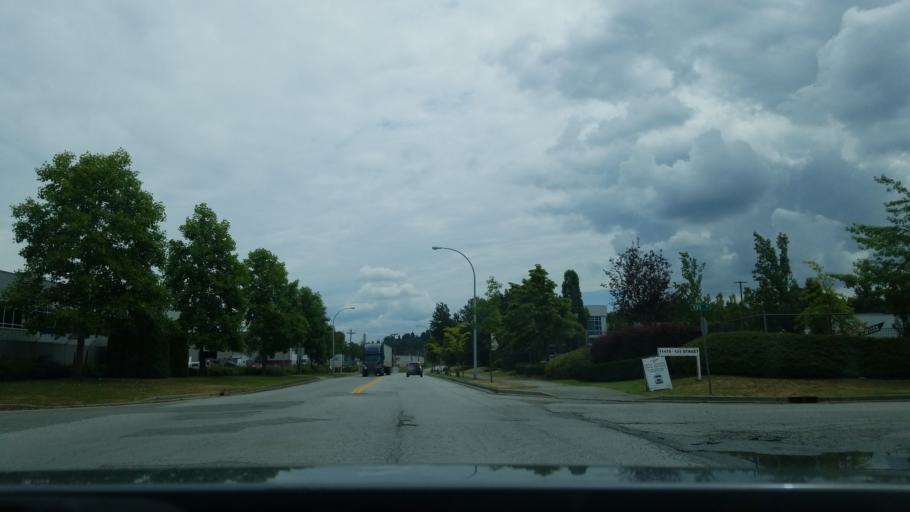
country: CA
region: British Columbia
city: New Westminster
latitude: 49.2112
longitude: -122.8594
